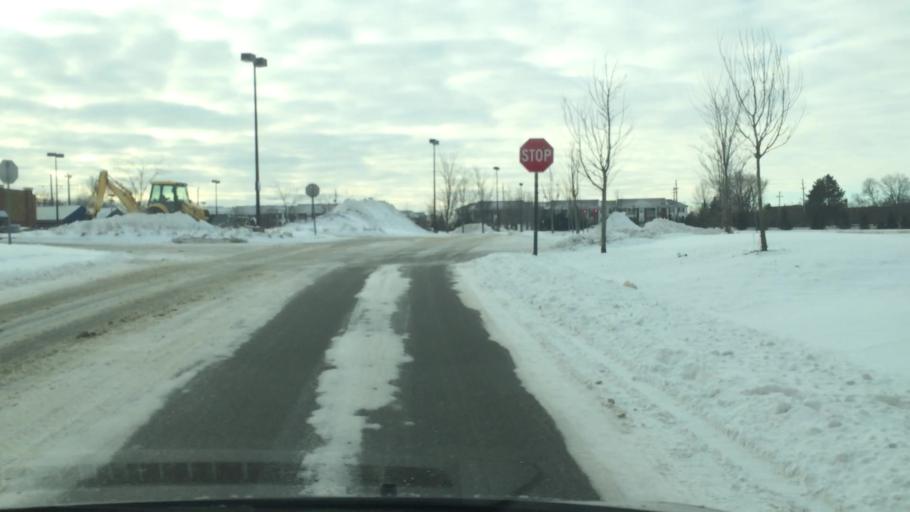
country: US
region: Ohio
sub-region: Cuyahoga County
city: Middleburg Heights
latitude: 41.3451
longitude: -81.8216
